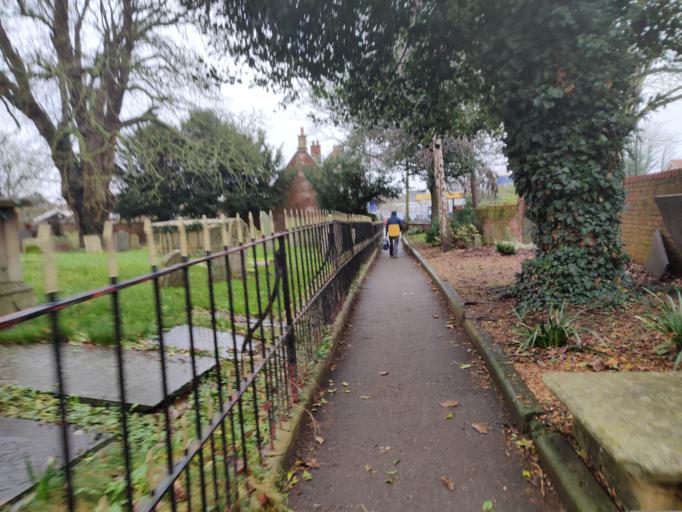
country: GB
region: England
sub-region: Lincolnshire
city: Bourne
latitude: 52.7662
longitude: -0.3758
